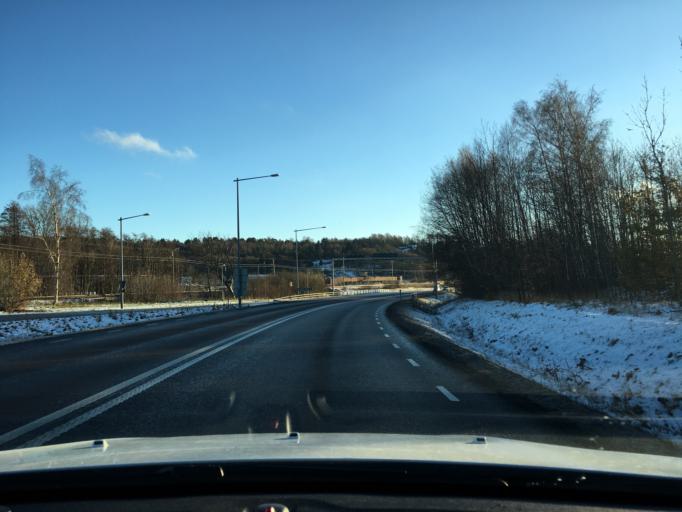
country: SE
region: Vaestra Goetaland
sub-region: Stenungsunds Kommun
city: Stenungsund
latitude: 58.0581
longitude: 11.8215
